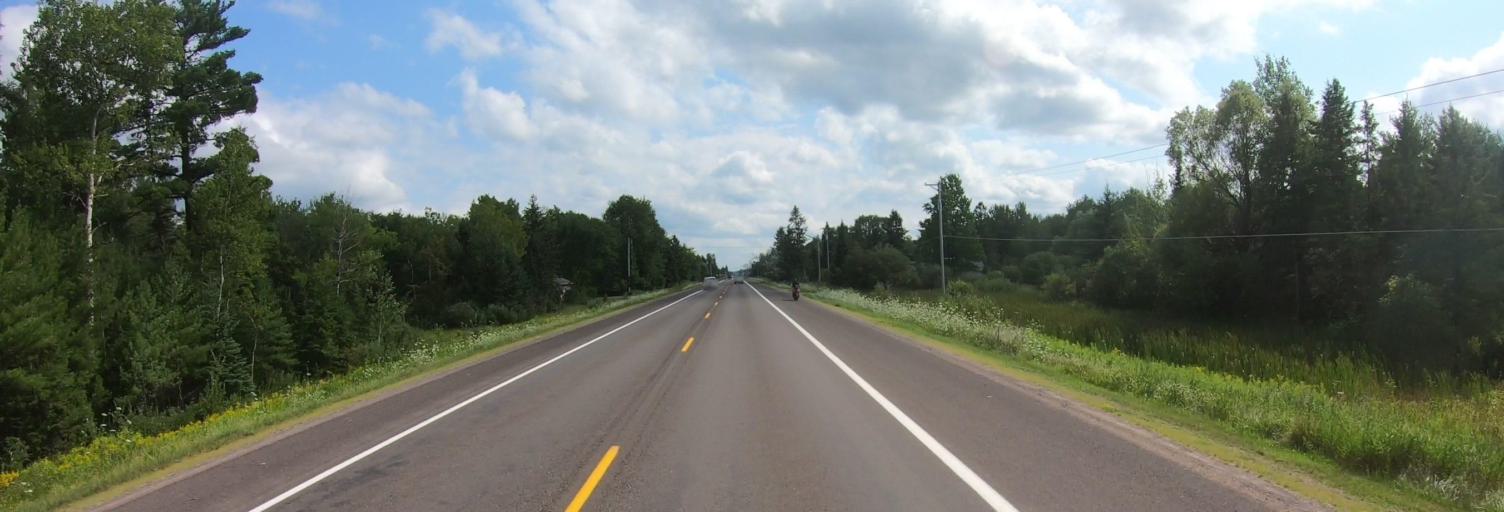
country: US
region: Michigan
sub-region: Ontonagon County
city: Ontonagon
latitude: 46.5432
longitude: -89.1785
